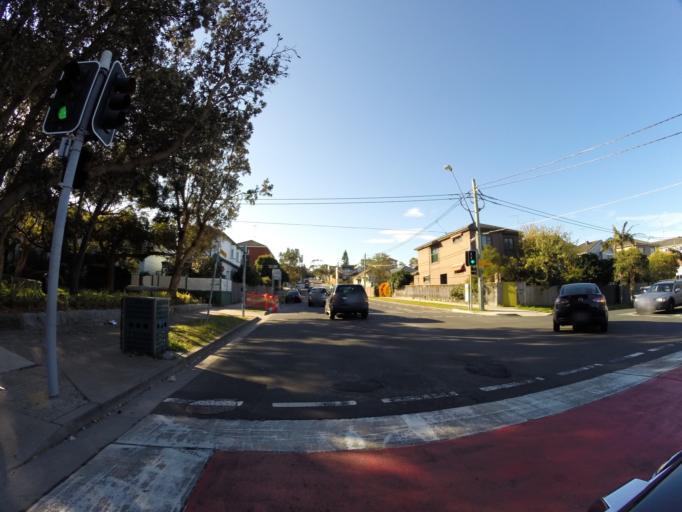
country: AU
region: New South Wales
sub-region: Waverley
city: Bronte
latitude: -33.9005
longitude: 151.2628
